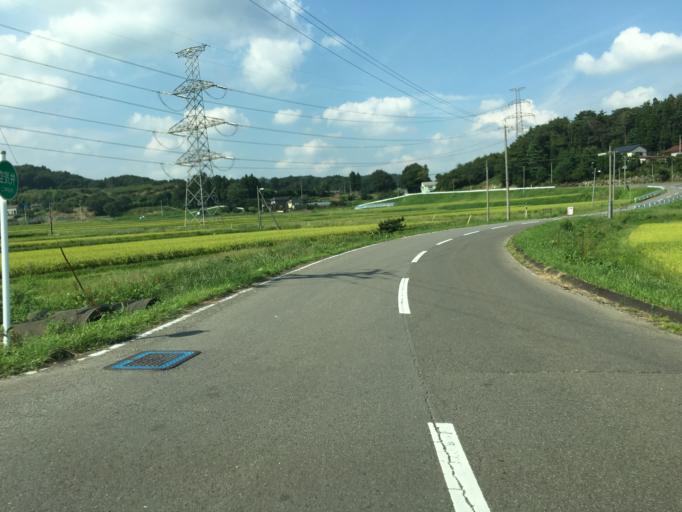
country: JP
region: Fukushima
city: Nihommatsu
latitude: 37.5754
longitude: 140.3838
